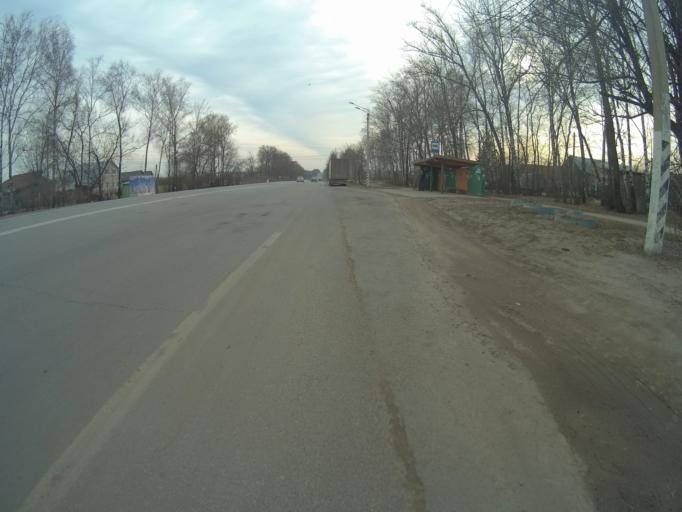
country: RU
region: Vladimir
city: Bogolyubovo
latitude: 56.1870
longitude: 40.5183
